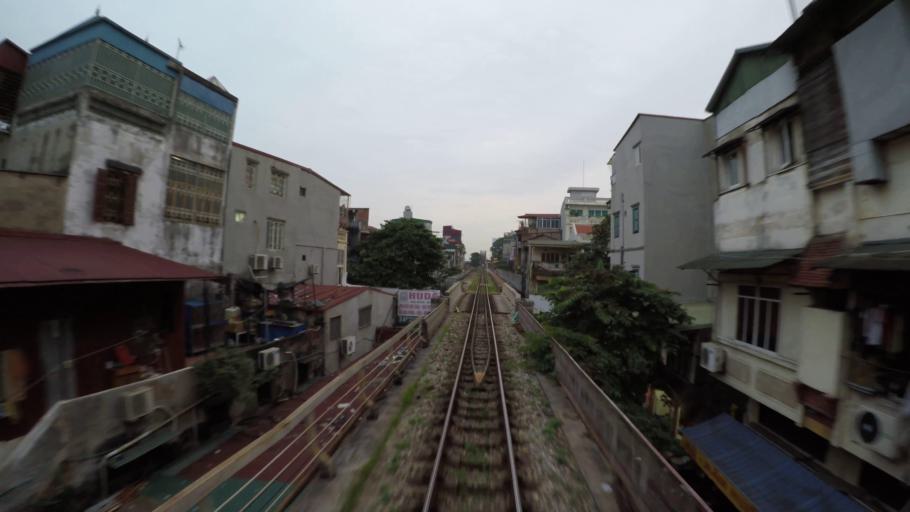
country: VN
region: Ha Noi
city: Hoan Kiem
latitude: 21.0454
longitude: 105.8638
